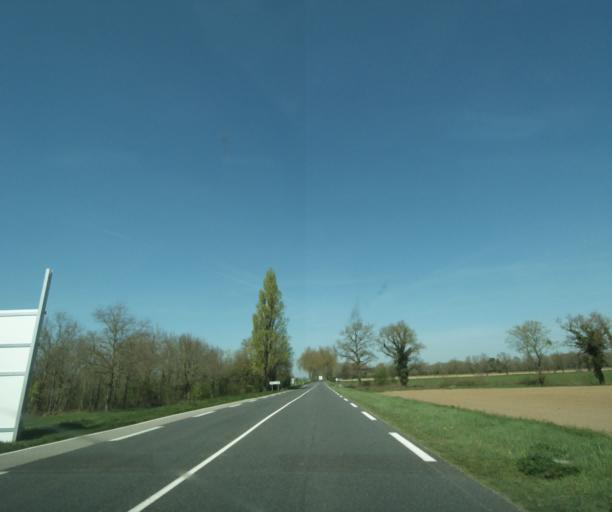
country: FR
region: Bourgogne
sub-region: Departement de la Nievre
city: Chantenay-Saint-Imbert
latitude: 46.6844
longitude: 3.2231
